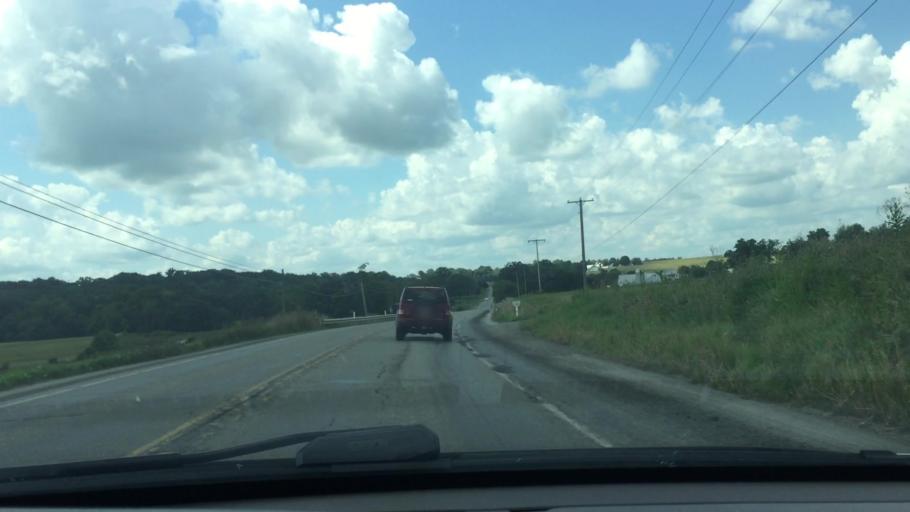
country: US
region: Pennsylvania
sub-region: Lawrence County
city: New Wilmington
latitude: 41.1167
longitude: -80.2766
